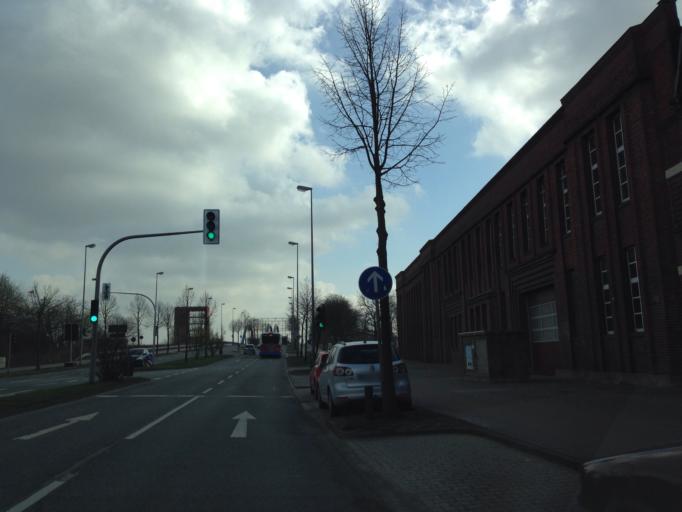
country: DE
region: North Rhine-Westphalia
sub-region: Regierungsbezirk Munster
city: Muenster
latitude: 51.9483
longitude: 7.6409
